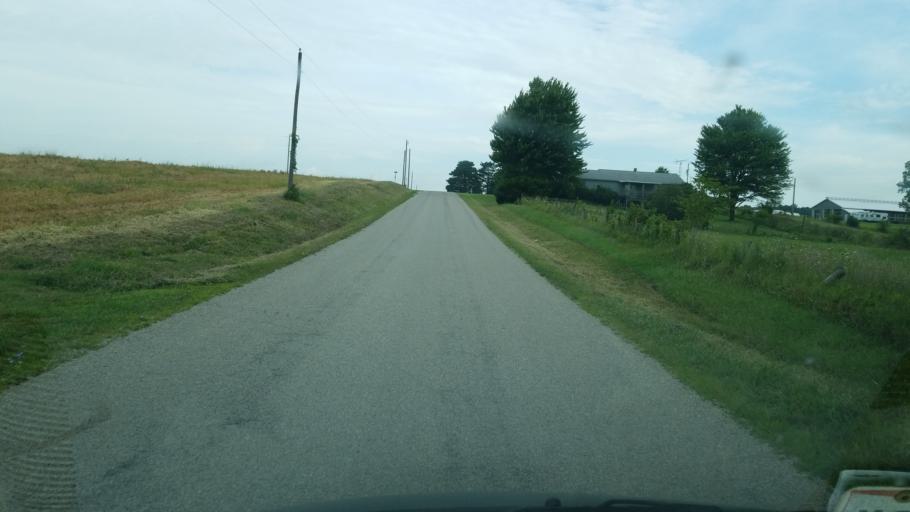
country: US
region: Ohio
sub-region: Seneca County
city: Tiffin
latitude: 41.0362
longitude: -83.0545
